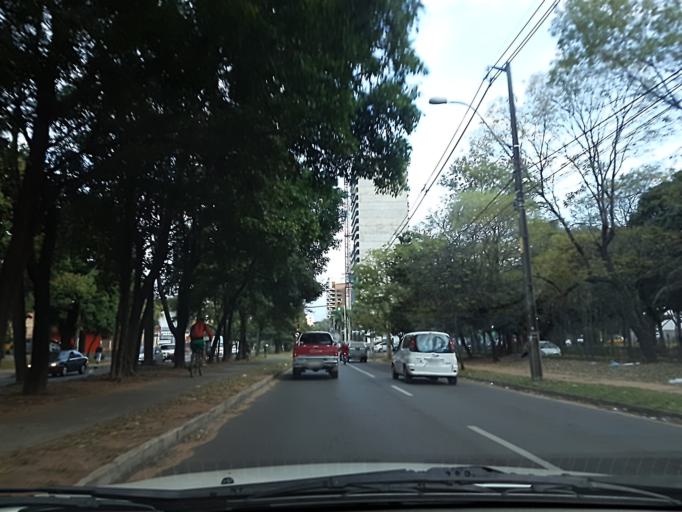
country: PY
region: Central
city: Fernando de la Mora
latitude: -25.2885
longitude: -57.5550
